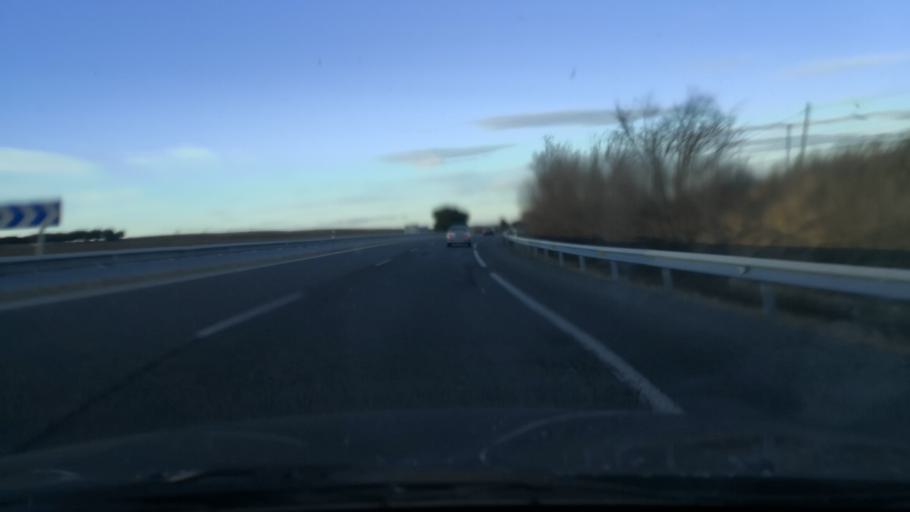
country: ES
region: Castille and Leon
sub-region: Provincia de Valladolid
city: Rueda
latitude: 41.3609
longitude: -4.9623
